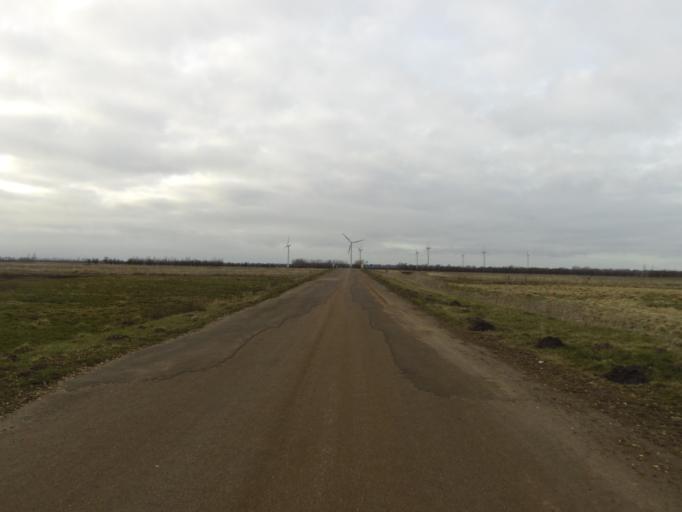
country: DK
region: South Denmark
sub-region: Tonder Kommune
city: Toftlund
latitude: 55.2390
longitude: 9.0724
